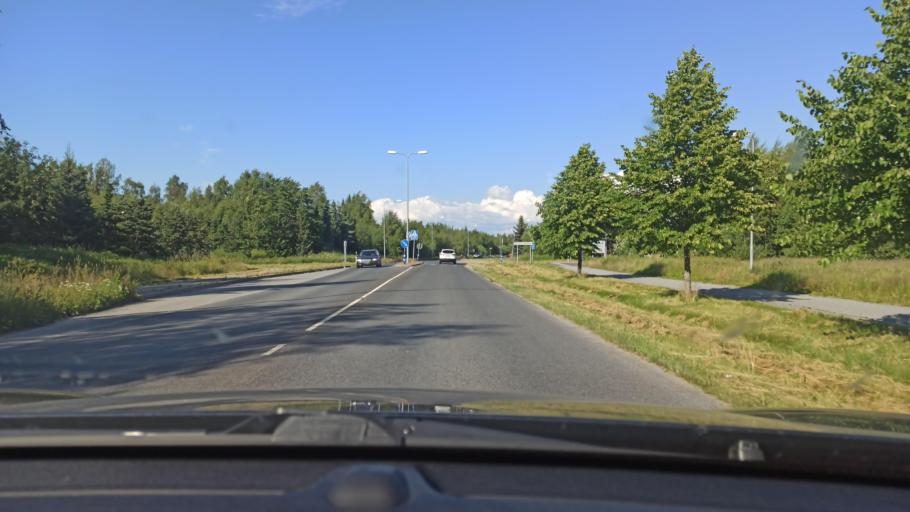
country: FI
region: Satakunta
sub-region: Pori
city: Pori
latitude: 61.4988
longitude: 21.8451
